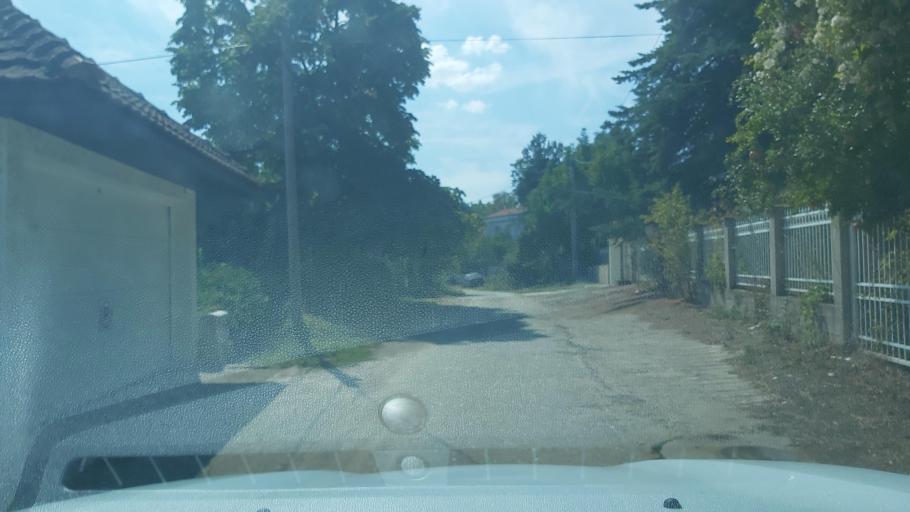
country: MK
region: Dojran
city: Star Dojran
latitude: 41.1827
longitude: 22.7216
